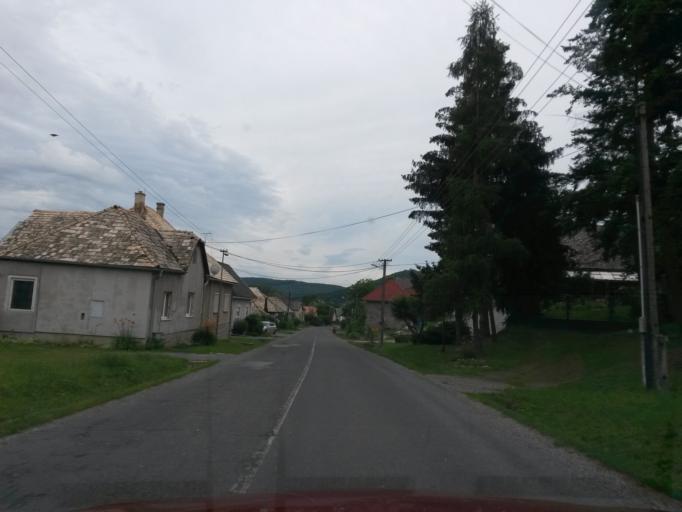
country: SK
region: Banskobystricky
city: Velky Krtis
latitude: 48.3108
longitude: 19.3961
